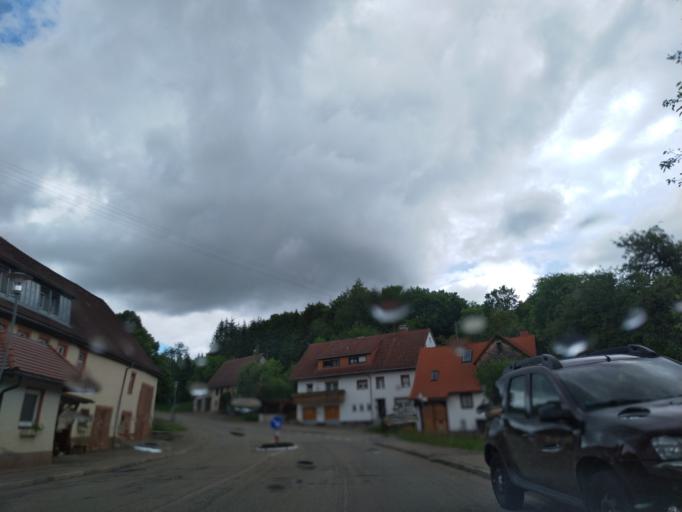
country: DE
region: Baden-Wuerttemberg
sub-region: Freiburg Region
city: Loffingen
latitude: 47.8589
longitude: 8.3125
